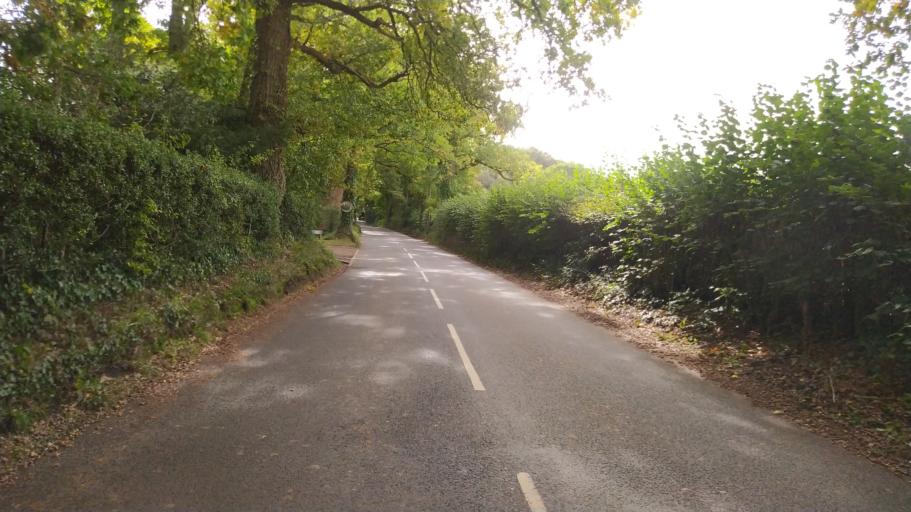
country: GB
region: England
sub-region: Hampshire
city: Romsey
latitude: 51.0217
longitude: -1.5415
